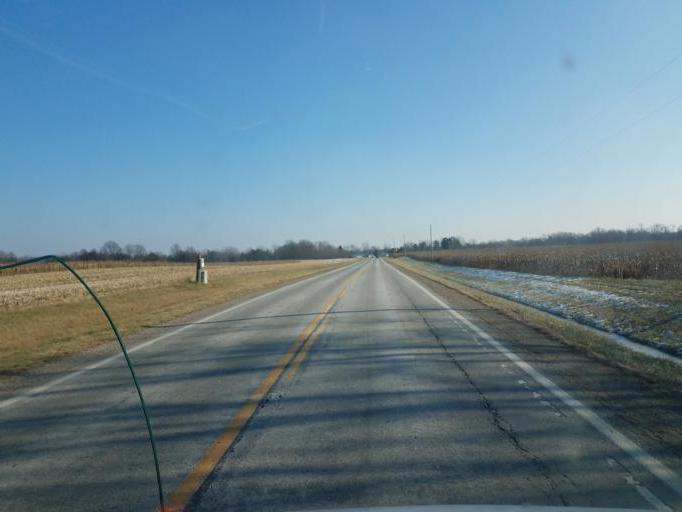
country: US
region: Ohio
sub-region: Morrow County
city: Cardington
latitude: 40.5090
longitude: -82.9120
